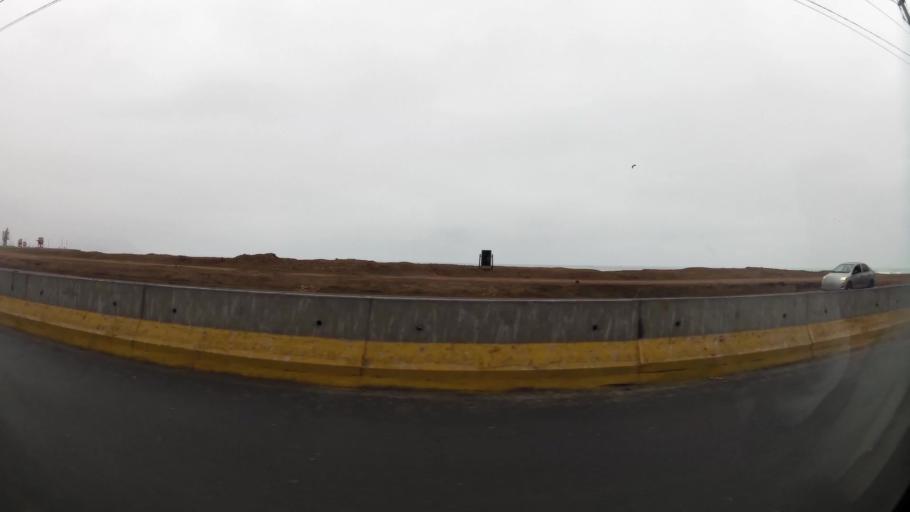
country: PE
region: Lima
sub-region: Lima
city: San Isidro
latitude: -12.1183
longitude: -77.0471
